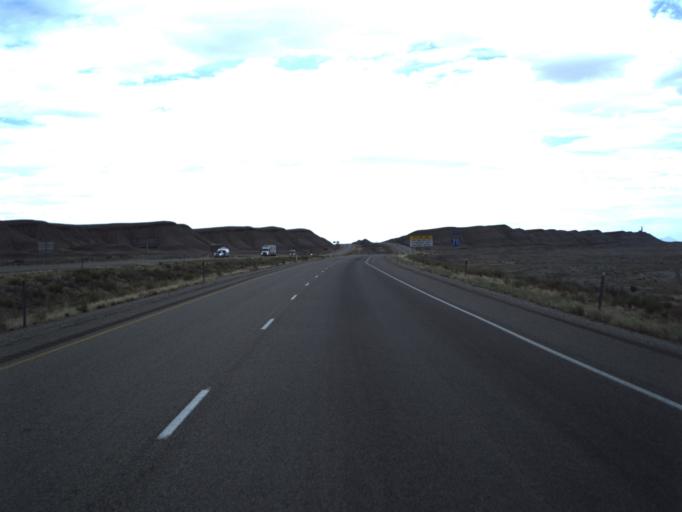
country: US
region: Utah
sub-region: Carbon County
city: East Carbon City
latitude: 38.9745
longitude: -110.1110
